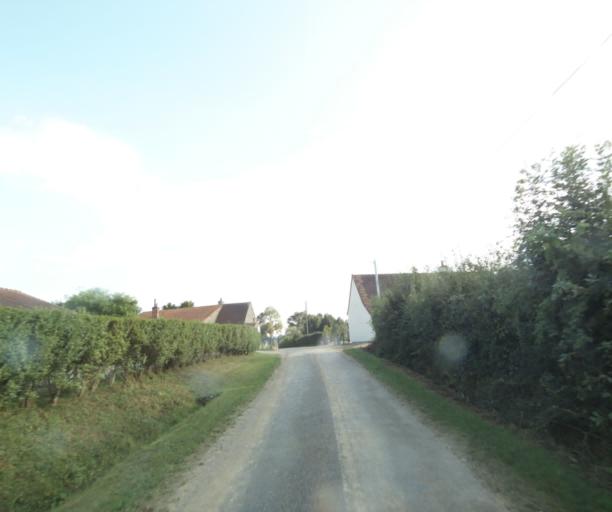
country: FR
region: Bourgogne
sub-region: Departement de Saone-et-Loire
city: Paray-le-Monial
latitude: 46.5251
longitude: 4.1220
